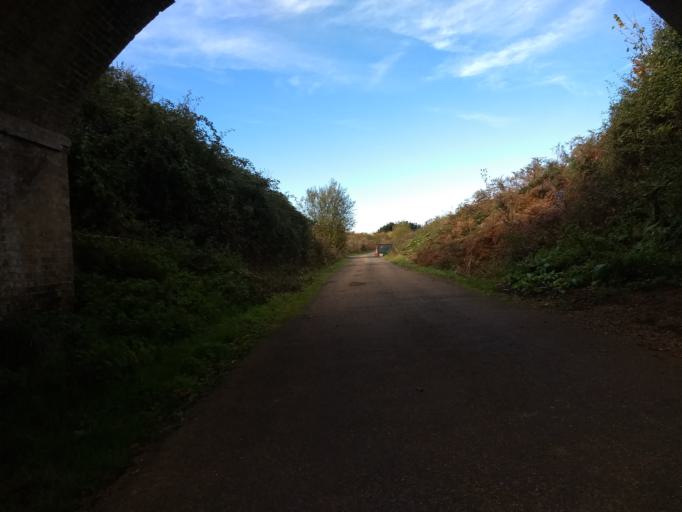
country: GB
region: England
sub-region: Isle of Wight
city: Newchurch
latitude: 50.6552
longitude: -1.2516
